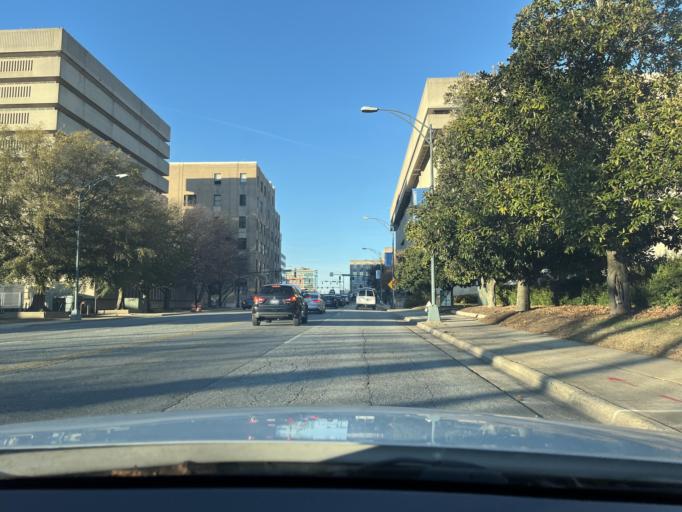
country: US
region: North Carolina
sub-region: Guilford County
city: Greensboro
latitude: 36.0708
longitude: -79.7939
